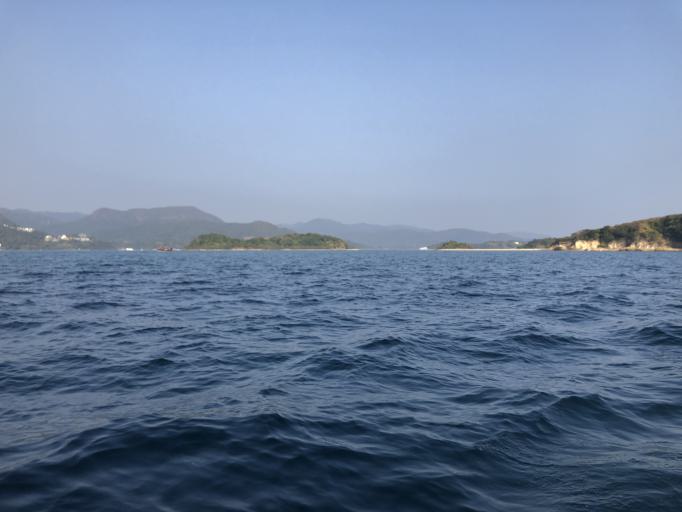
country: HK
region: Sai Kung
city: Sai Kung
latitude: 22.3749
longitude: 114.2809
